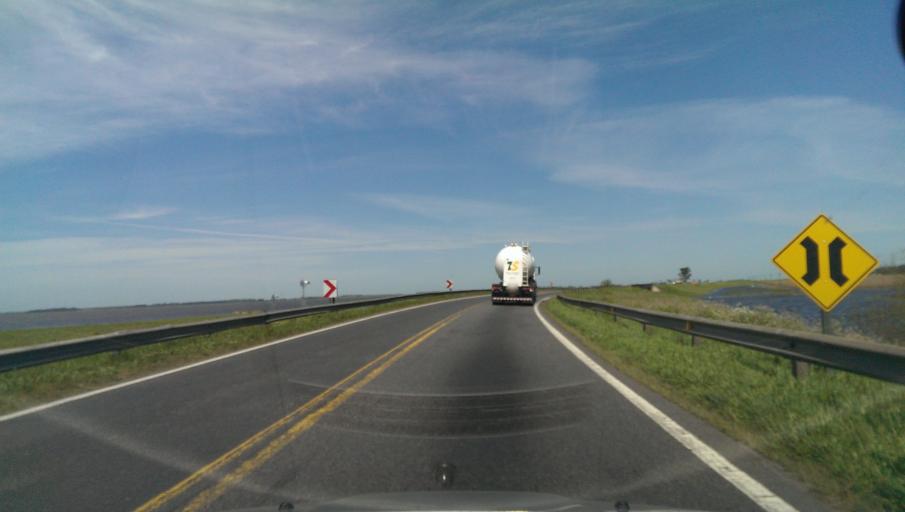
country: AR
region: Buenos Aires
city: San Miguel del Monte
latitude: -35.6633
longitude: -58.8512
